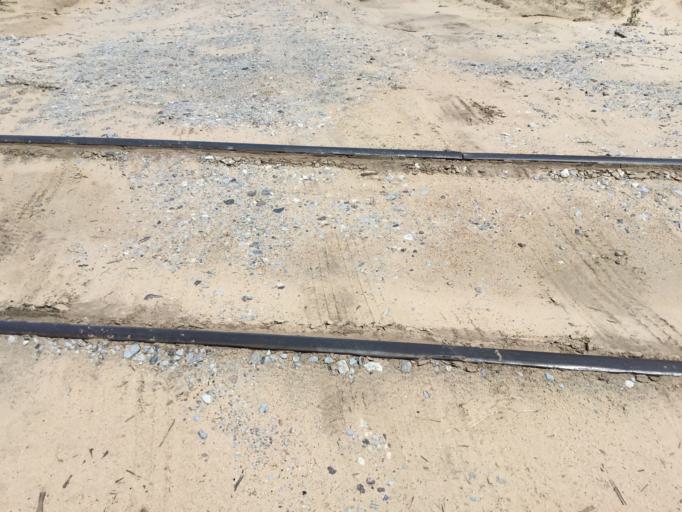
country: US
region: Kansas
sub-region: Barber County
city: Medicine Lodge
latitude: 37.4443
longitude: -98.4465
